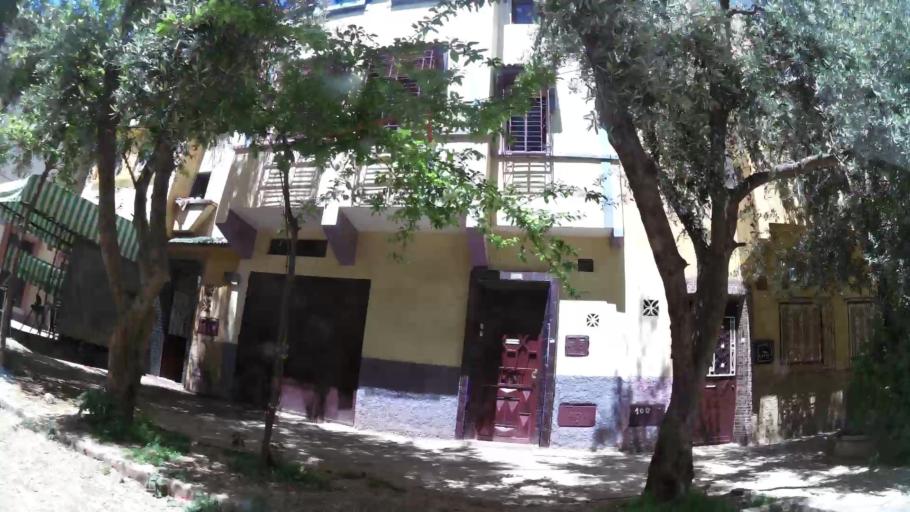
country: MA
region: Meknes-Tafilalet
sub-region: Meknes
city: Meknes
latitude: 33.9058
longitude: -5.5772
